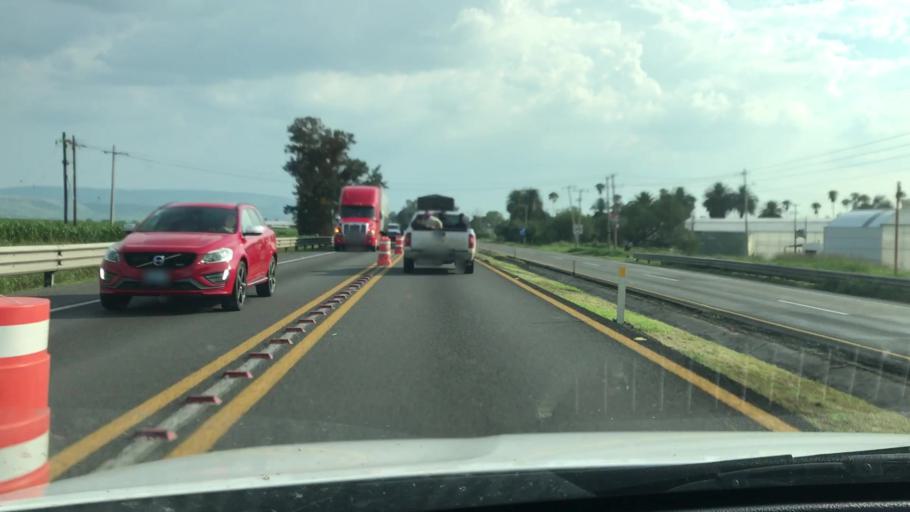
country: MX
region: Guanajuato
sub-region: Irapuato
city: San Ignacio de Rivera (Ojo de Agua)
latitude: 20.5119
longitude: -101.4698
